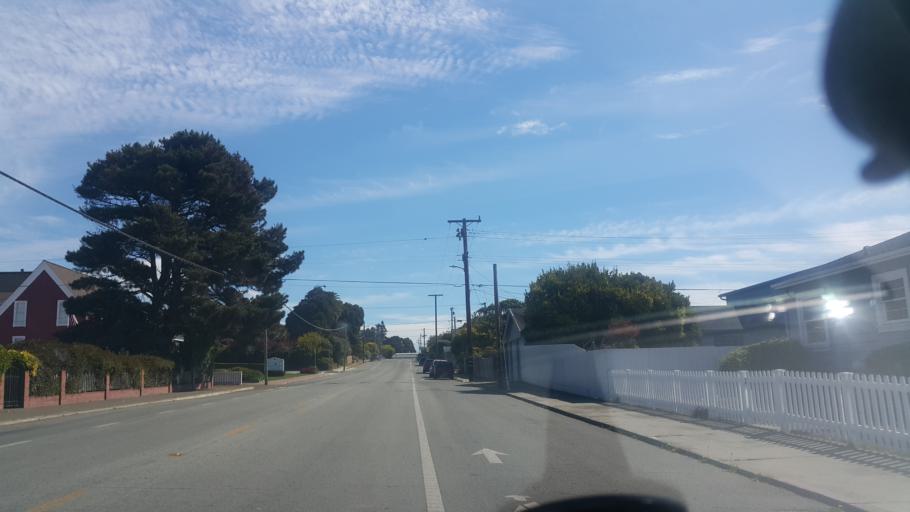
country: US
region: California
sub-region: Mendocino County
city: Fort Bragg
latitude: 39.4480
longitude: -123.8020
